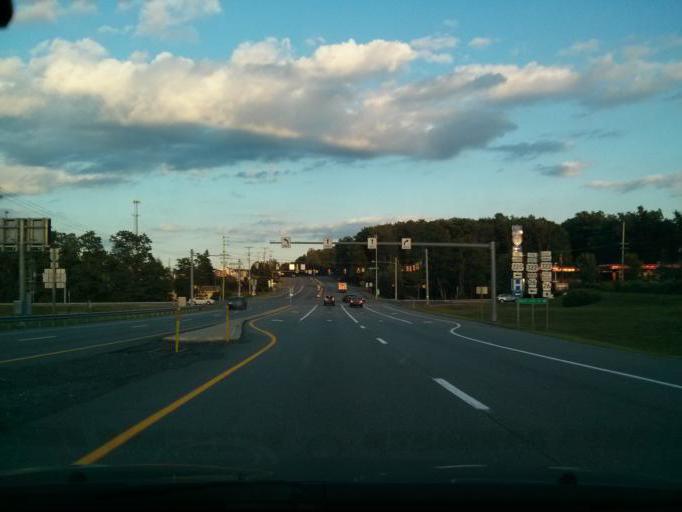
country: US
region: Pennsylvania
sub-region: Centre County
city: Park Forest Village
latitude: 40.8126
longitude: -77.9239
